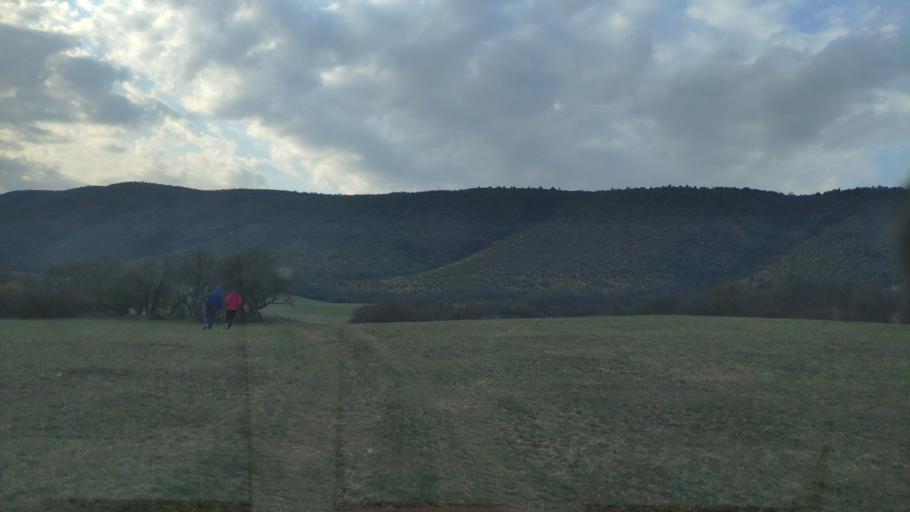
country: SK
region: Kosicky
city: Medzev
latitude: 48.6213
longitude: 20.9070
